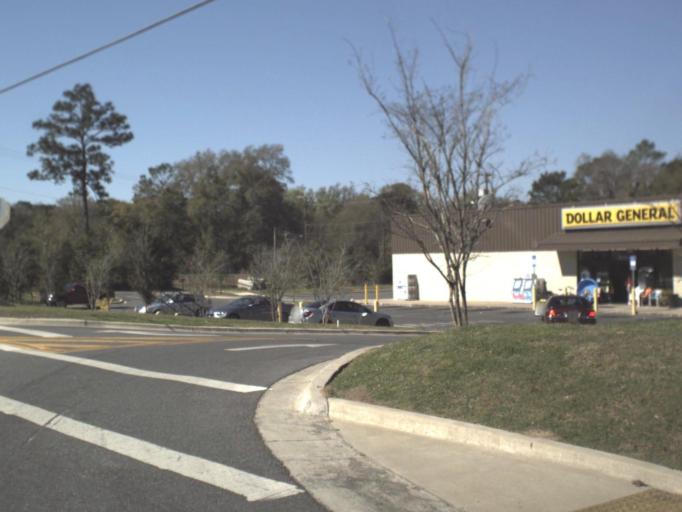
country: US
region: Florida
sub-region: Leon County
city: Tallahassee
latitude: 30.3815
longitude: -84.2899
